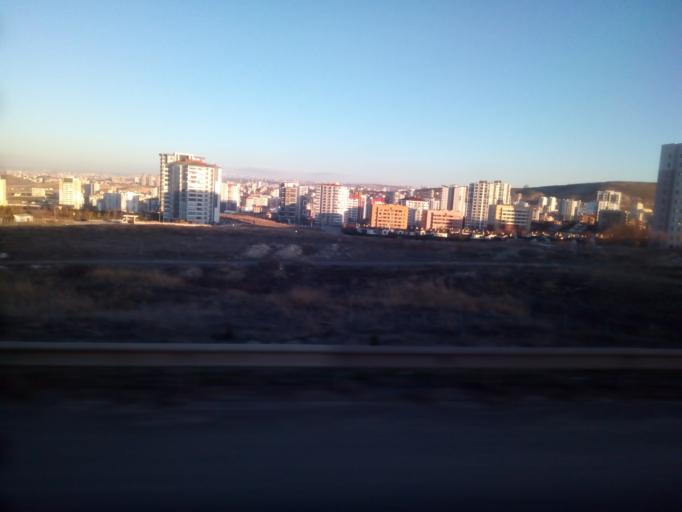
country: TR
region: Ankara
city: Etimesgut
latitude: 39.9033
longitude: 32.6251
